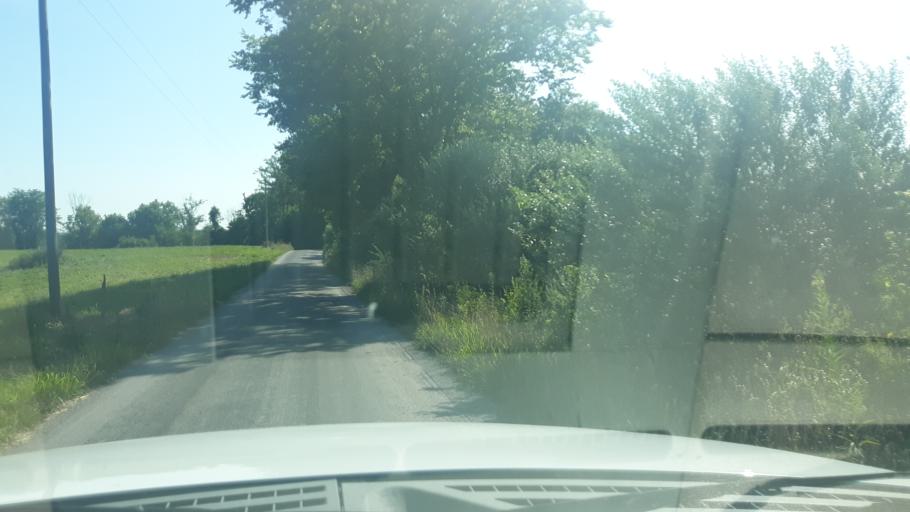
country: US
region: Illinois
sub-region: Saline County
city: Harrisburg
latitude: 37.8520
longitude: -88.5998
